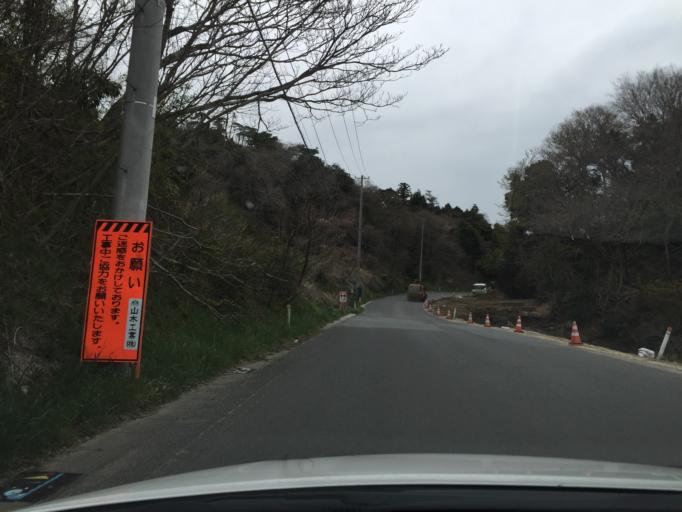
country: JP
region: Fukushima
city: Iwaki
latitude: 37.0052
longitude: 140.9674
